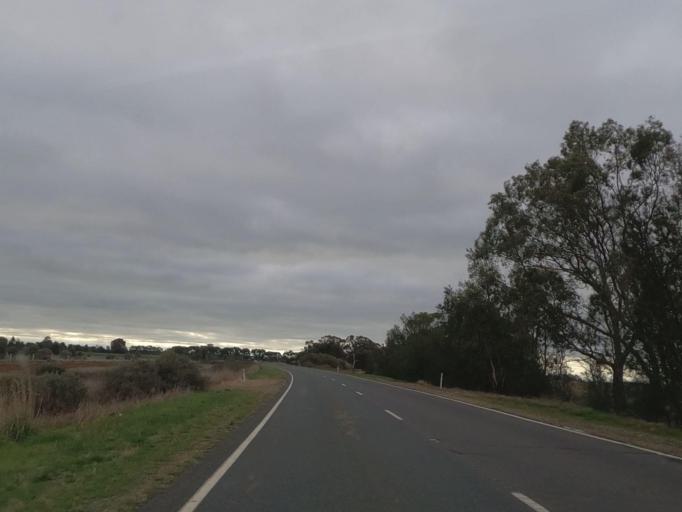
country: AU
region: Victoria
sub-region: Swan Hill
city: Swan Hill
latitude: -35.9458
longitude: 143.9396
